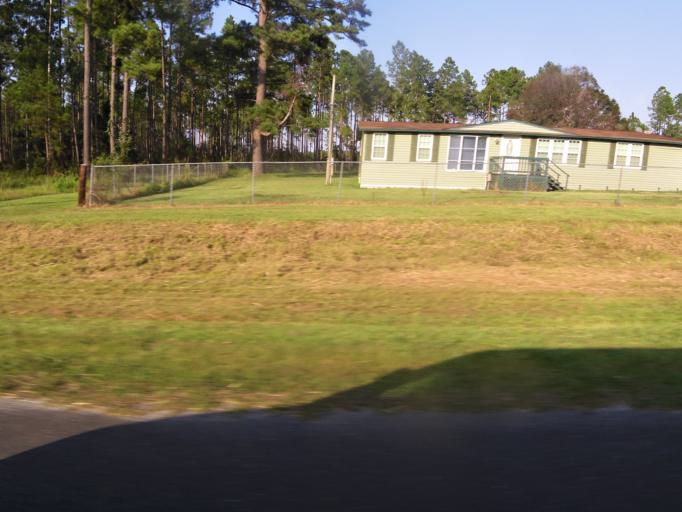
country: US
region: Florida
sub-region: Duval County
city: Baldwin
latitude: 30.3658
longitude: -82.0131
